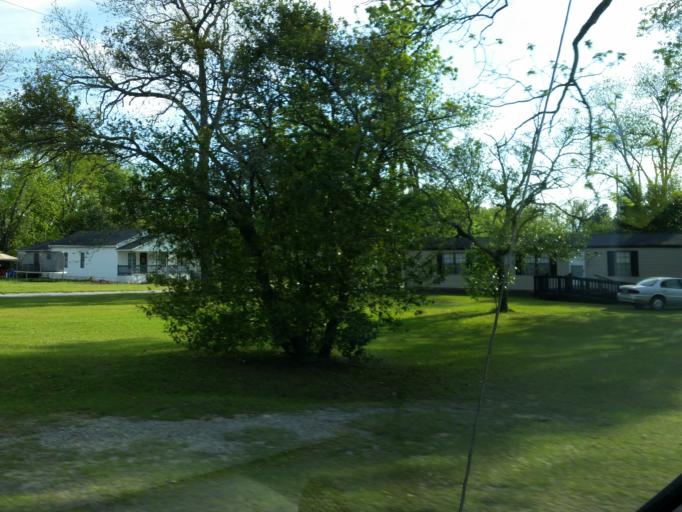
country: US
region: Georgia
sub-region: Crisp County
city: Cordele
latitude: 31.9765
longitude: -83.7882
